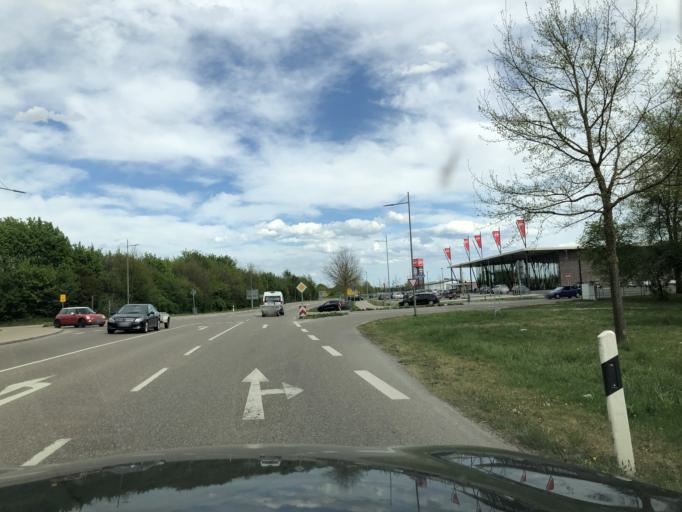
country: DE
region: Bavaria
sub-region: Swabia
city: Asbach-Baumenheim
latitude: 48.6740
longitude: 10.8200
